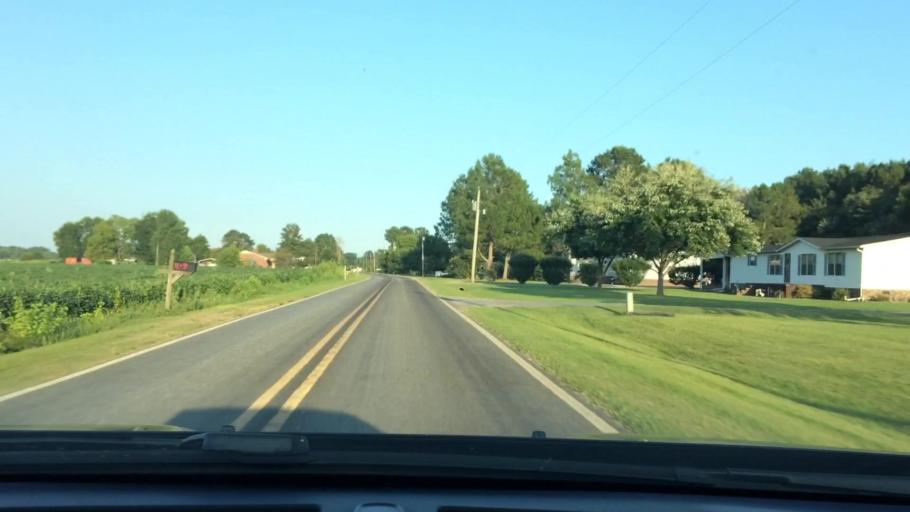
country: US
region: North Carolina
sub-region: Pitt County
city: Ayden
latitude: 35.4312
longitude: -77.4475
